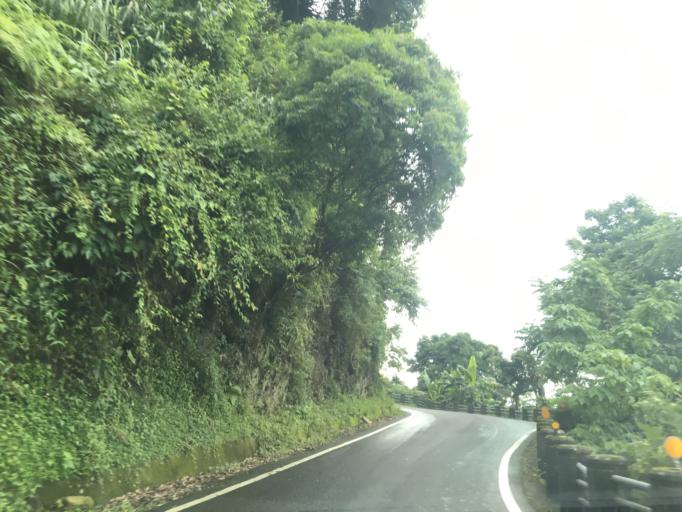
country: TW
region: Taiwan
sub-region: Chiayi
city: Jiayi Shi
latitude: 23.4441
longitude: 120.6600
